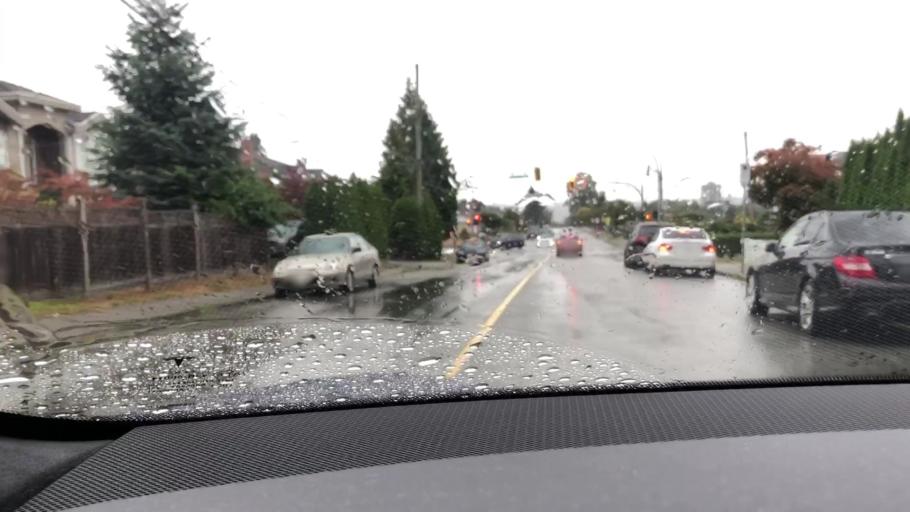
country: CA
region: British Columbia
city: New Westminster
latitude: 49.2280
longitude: -122.9130
